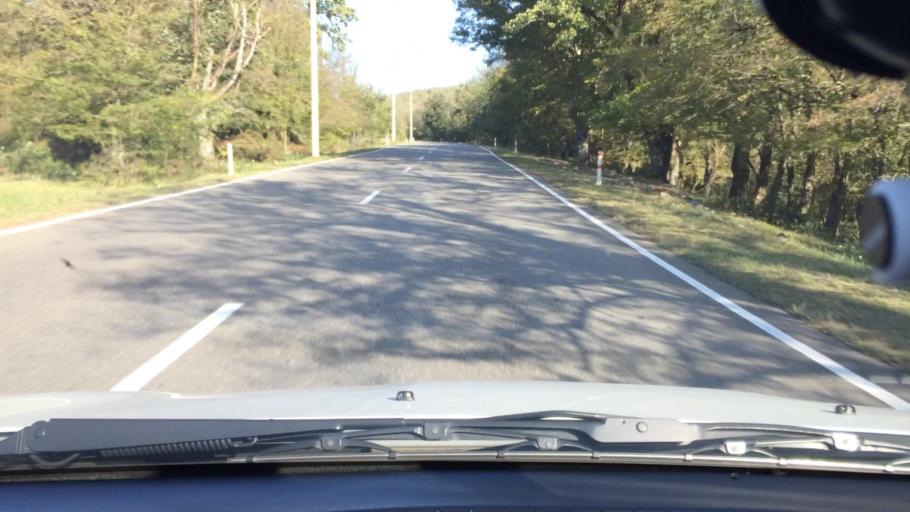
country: GE
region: Imereti
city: Kutaisi
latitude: 42.2480
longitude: 42.7559
